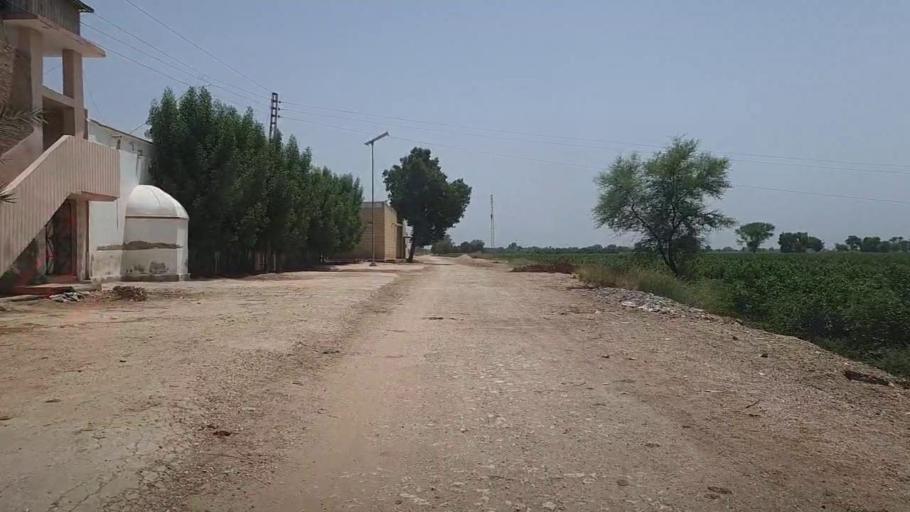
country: PK
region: Sindh
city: Pad Idan
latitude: 26.8434
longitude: 68.3247
